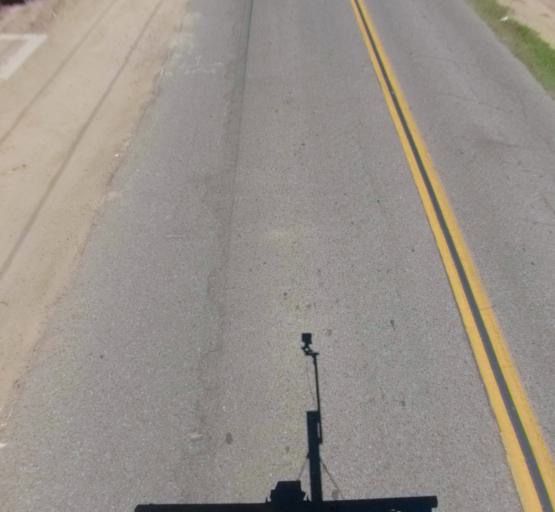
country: US
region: California
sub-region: Madera County
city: Chowchilla
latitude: 37.0562
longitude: -120.3200
